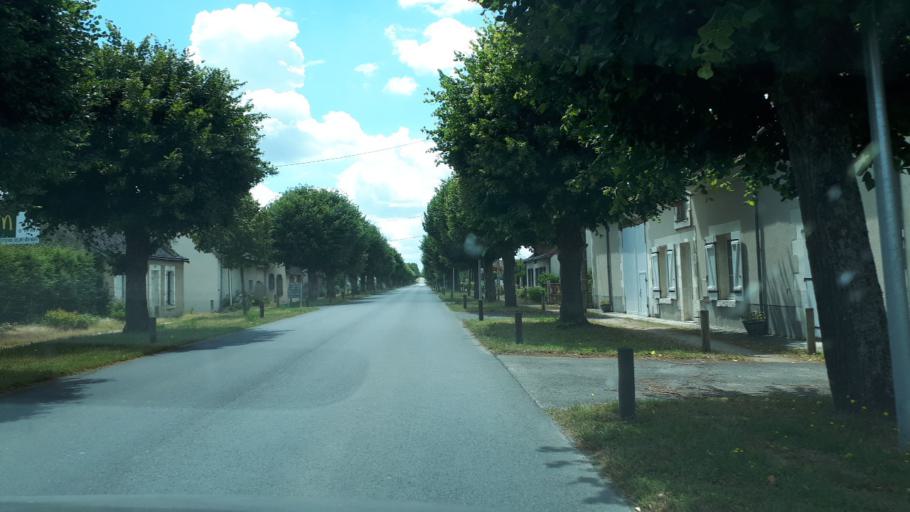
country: FR
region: Centre
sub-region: Departement du Loir-et-Cher
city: Contres
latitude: 47.4135
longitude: 1.4260
